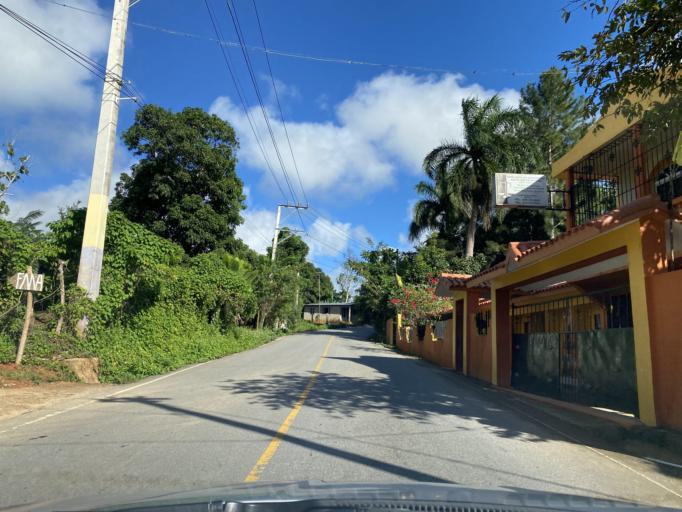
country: DO
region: Samana
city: Sanchez
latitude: 19.2550
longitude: -69.5767
